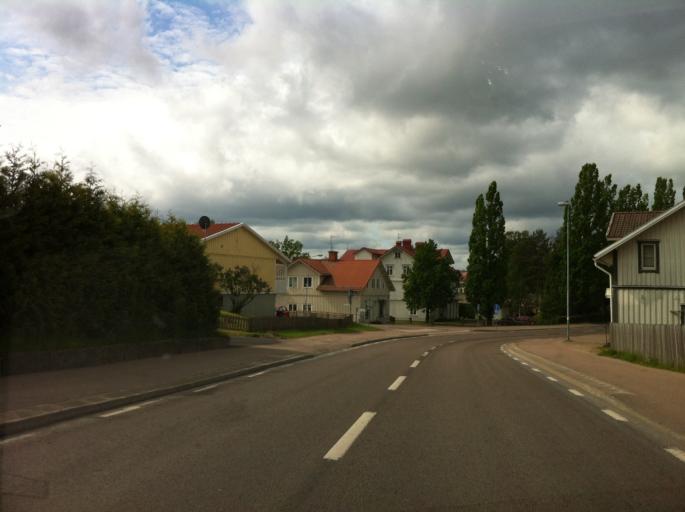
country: SE
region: Vaermland
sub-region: Sunne Kommun
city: Sunne
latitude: 59.8394
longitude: 13.1519
